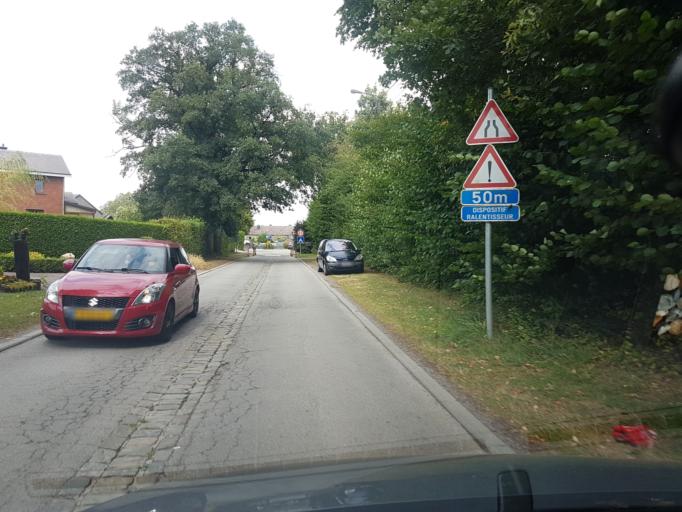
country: BE
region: Wallonia
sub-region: Province du Luxembourg
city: Manhay
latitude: 50.2902
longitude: 5.6743
